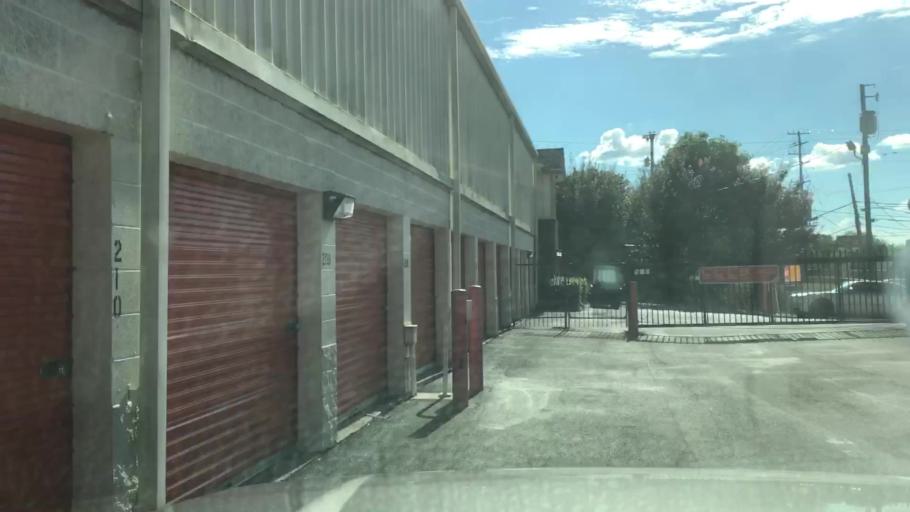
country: US
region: Tennessee
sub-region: Davidson County
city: Belle Meade
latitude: 36.1473
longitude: -86.8686
